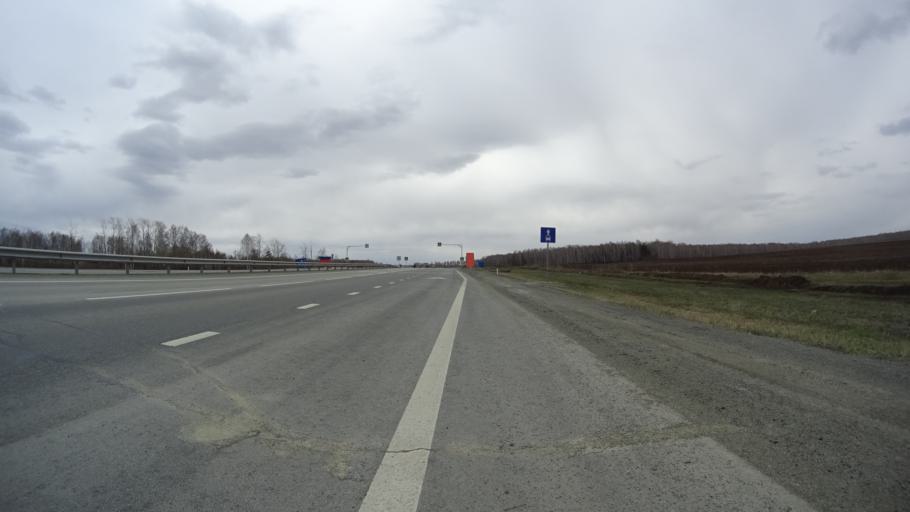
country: RU
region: Chelyabinsk
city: Yemanzhelinka
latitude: 54.8248
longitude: 61.3097
